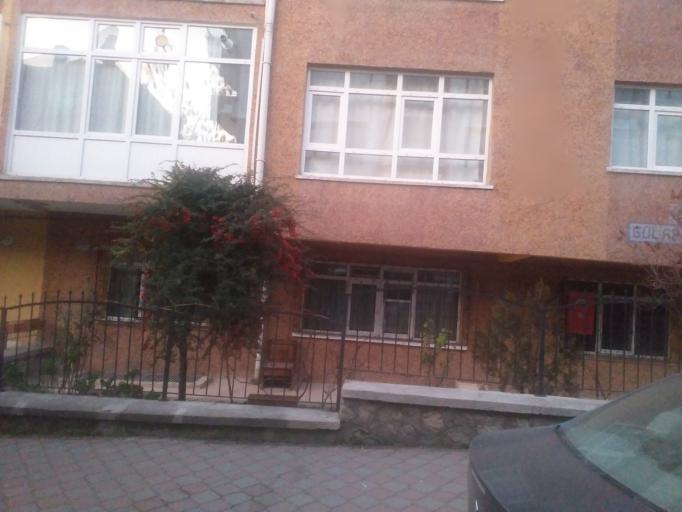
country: TR
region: Ankara
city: Ankara
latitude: 39.9754
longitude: 32.8399
